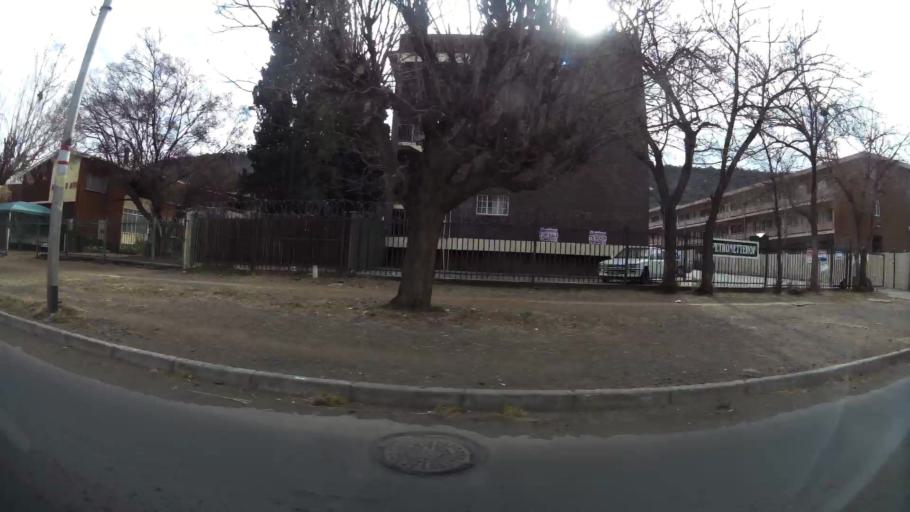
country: ZA
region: Orange Free State
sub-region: Mangaung Metropolitan Municipality
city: Bloemfontein
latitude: -29.1043
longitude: 26.2383
